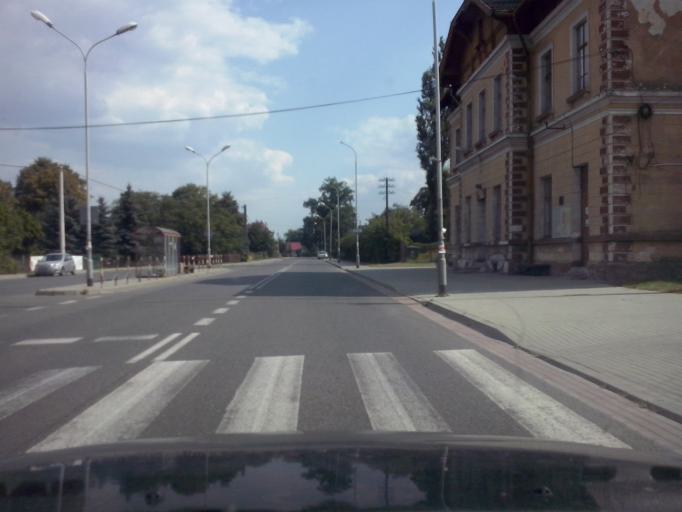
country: PL
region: Subcarpathian Voivodeship
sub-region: Powiat nizanski
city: Nisko
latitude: 50.5139
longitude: 22.1423
